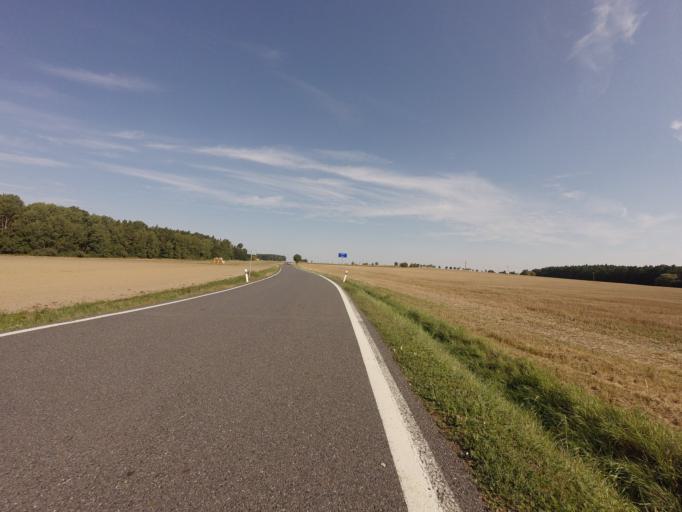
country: CZ
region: Jihocesky
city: Bernartice
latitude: 49.3156
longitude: 14.3723
